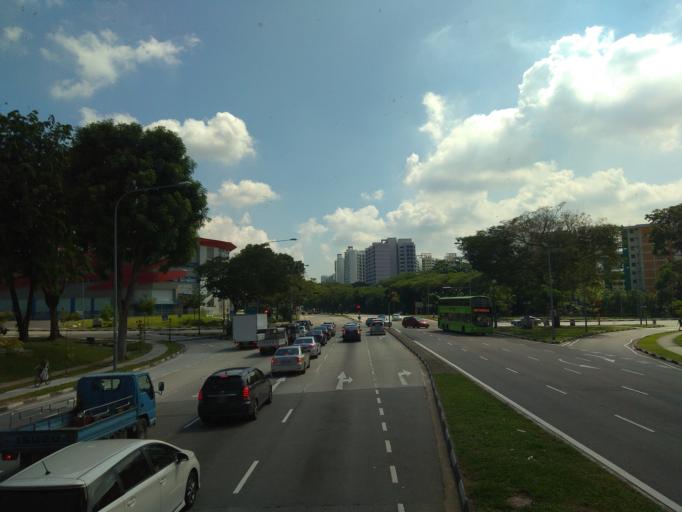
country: MY
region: Johor
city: Johor Bahru
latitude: 1.3468
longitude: 103.7044
